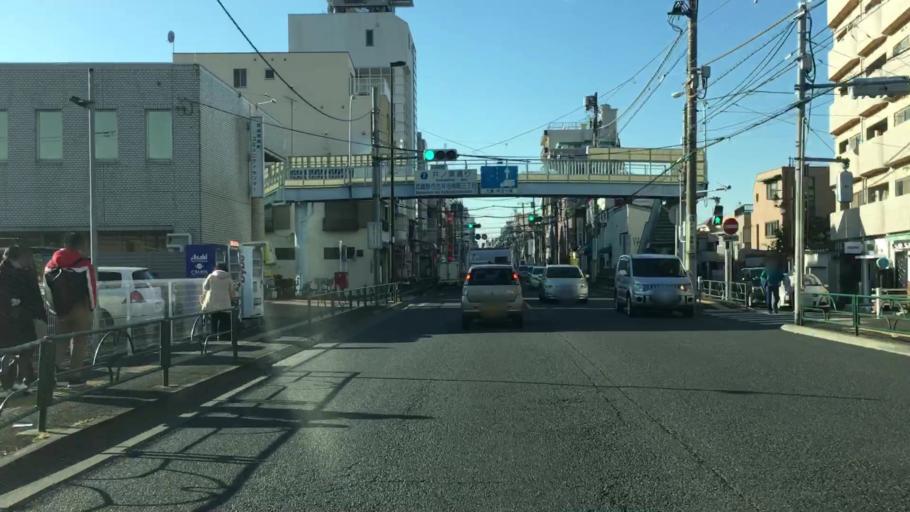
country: JP
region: Tokyo
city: Musashino
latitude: 35.6994
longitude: 139.5871
